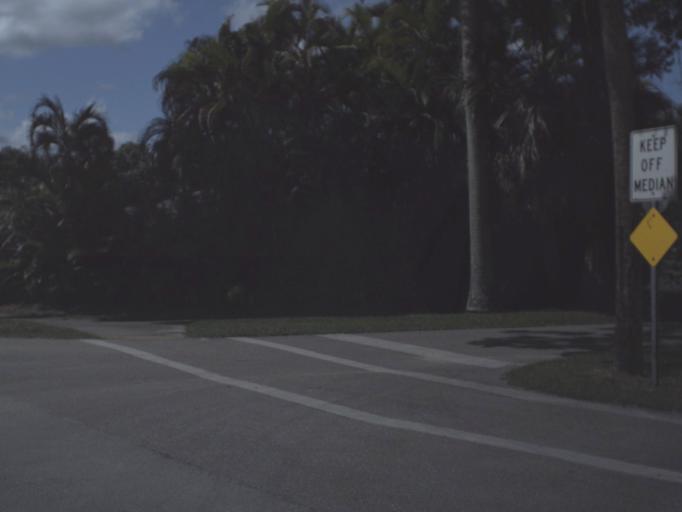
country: US
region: Florida
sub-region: Lee County
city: Whiskey Creek
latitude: 26.5896
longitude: -81.8937
